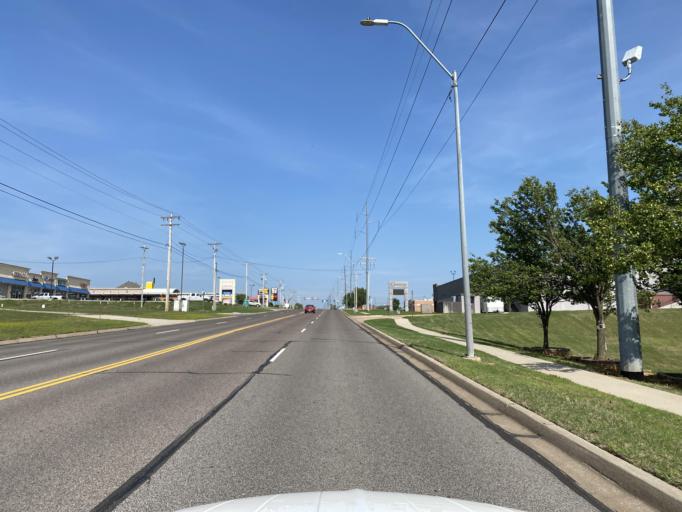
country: US
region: Oklahoma
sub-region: Oklahoma County
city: Midwest City
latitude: 35.4496
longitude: -97.3563
